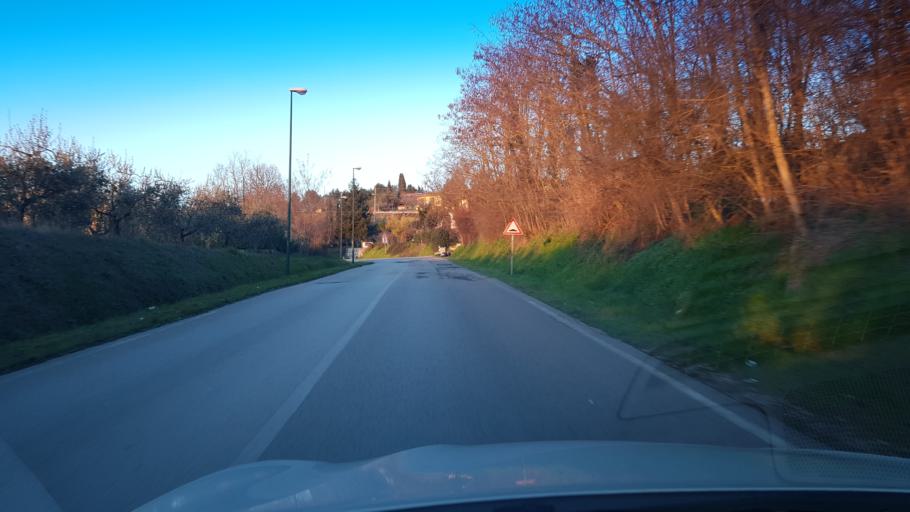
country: IT
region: Umbria
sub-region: Provincia di Perugia
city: Torgiano
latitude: 43.0126
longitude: 12.4354
